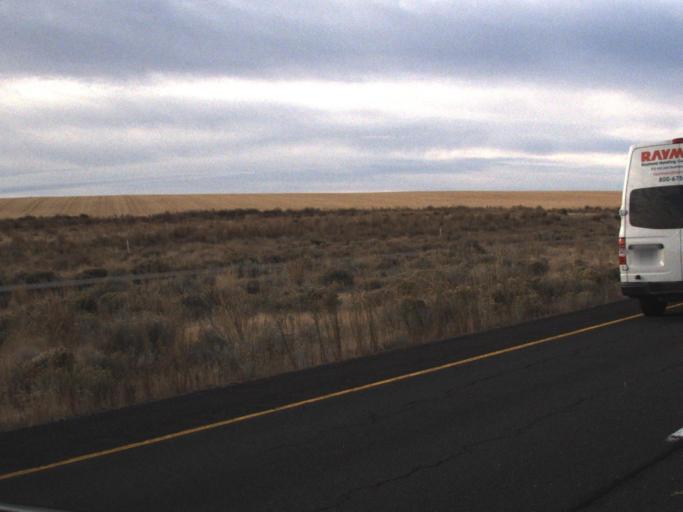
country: US
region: Washington
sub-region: Franklin County
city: Connell
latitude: 46.7894
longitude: -118.7525
